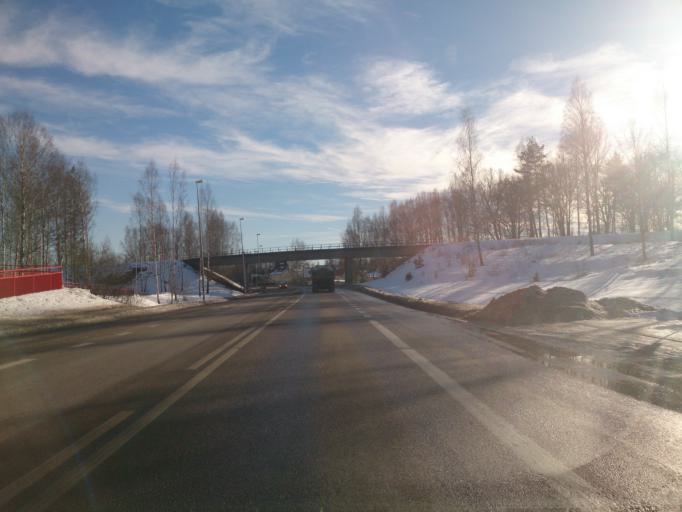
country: SE
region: OEstergoetland
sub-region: Atvidabergs Kommun
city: Atvidaberg
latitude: 58.2076
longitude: 15.9906
